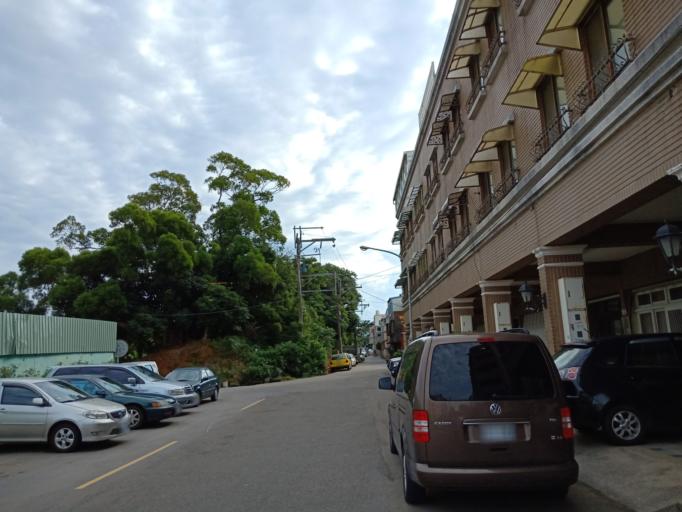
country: TW
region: Taiwan
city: Taoyuan City
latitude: 24.9486
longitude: 121.2621
